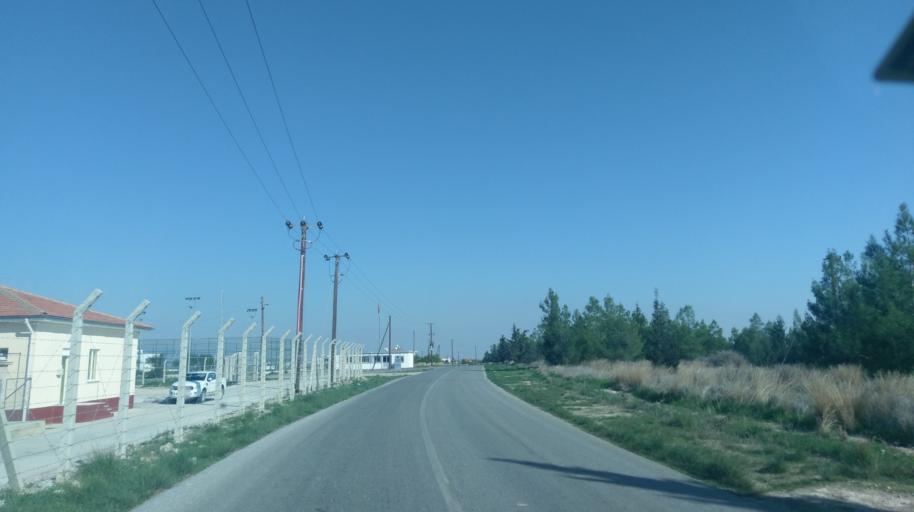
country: CY
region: Larnaka
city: Athienou
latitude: 35.1645
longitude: 33.5257
